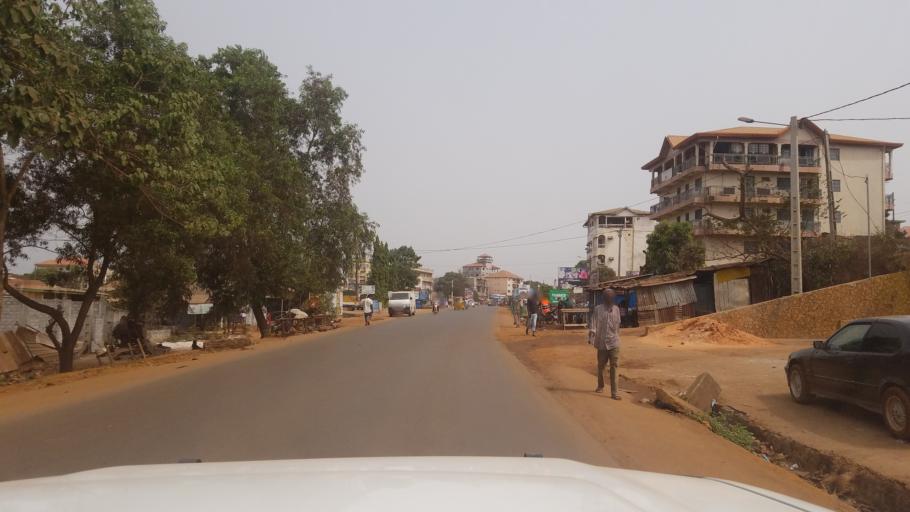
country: GN
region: Conakry
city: Conakry
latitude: 9.6496
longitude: -13.6025
